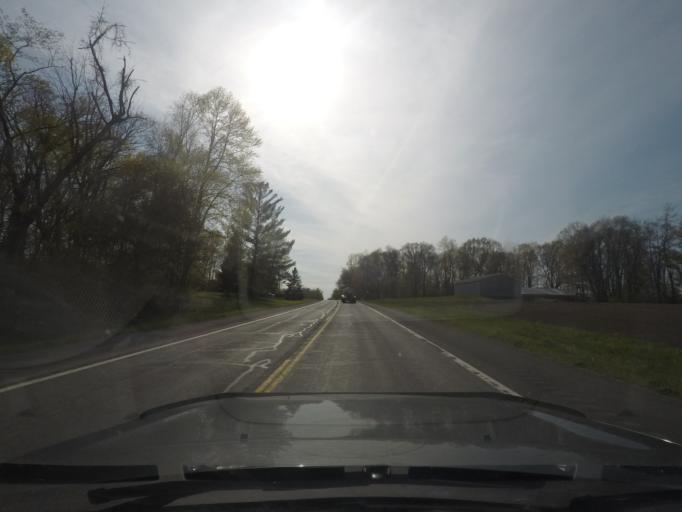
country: US
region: Michigan
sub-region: Berrien County
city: Buchanan
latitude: 41.7980
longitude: -86.4631
